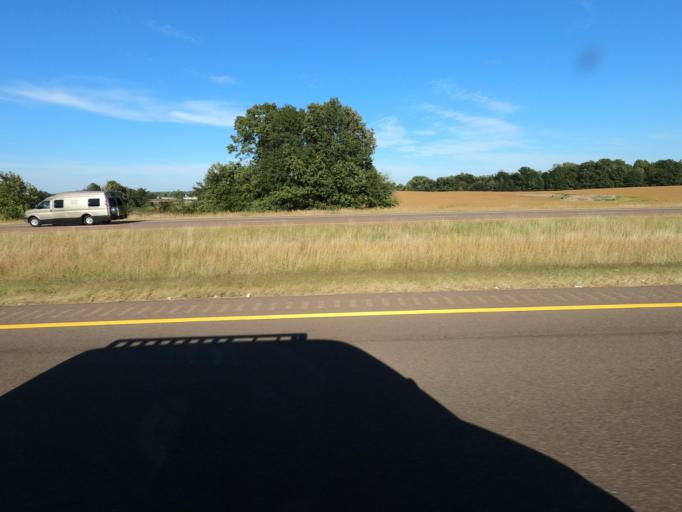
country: US
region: Tennessee
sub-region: Dyer County
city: Dyersburg
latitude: 35.9505
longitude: -89.3124
